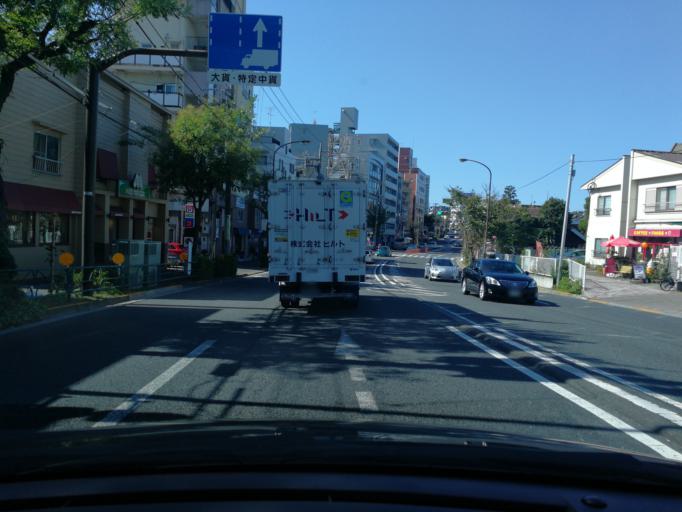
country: JP
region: Kanagawa
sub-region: Kawasaki-shi
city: Kawasaki
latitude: 35.6003
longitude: 139.6923
